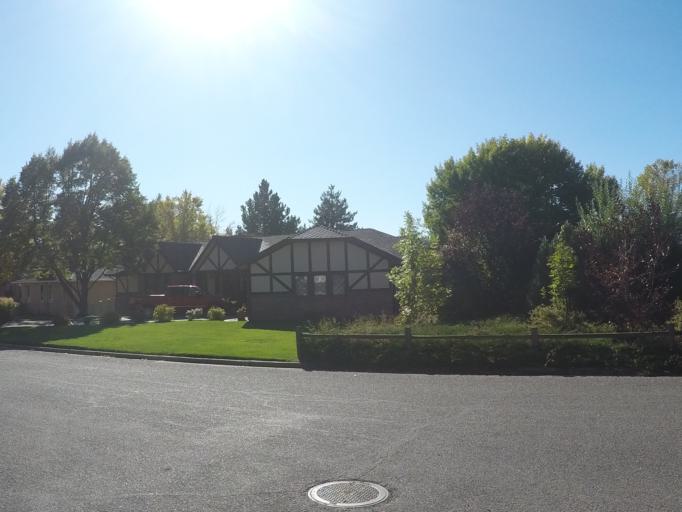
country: US
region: Montana
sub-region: Yellowstone County
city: Billings
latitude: 45.8001
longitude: -108.5876
